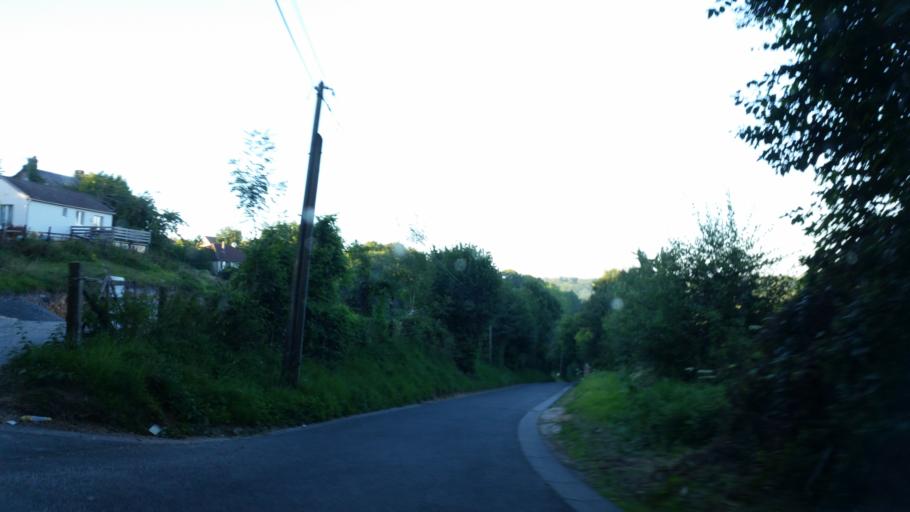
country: FR
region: Lower Normandy
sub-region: Departement du Calvados
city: Equemauville
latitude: 49.3977
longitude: 0.2144
